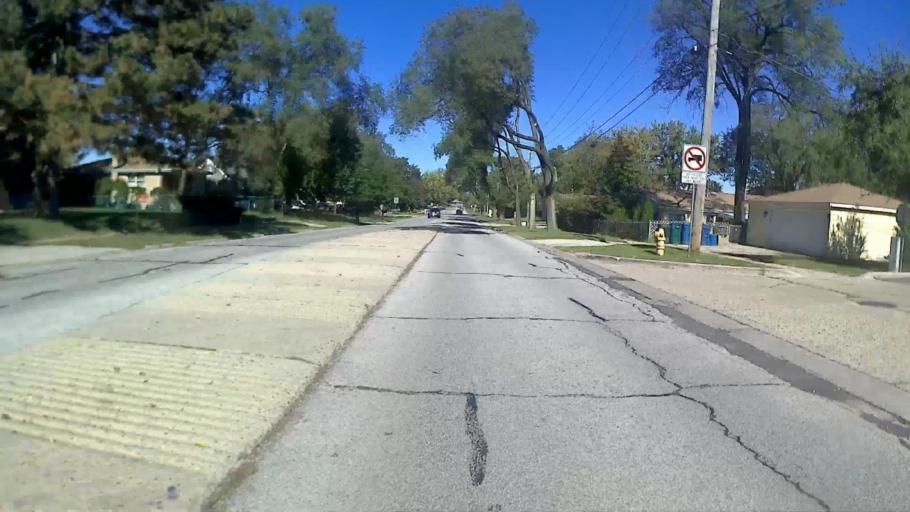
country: US
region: Illinois
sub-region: DuPage County
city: Addison
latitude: 41.9402
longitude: -88.0033
